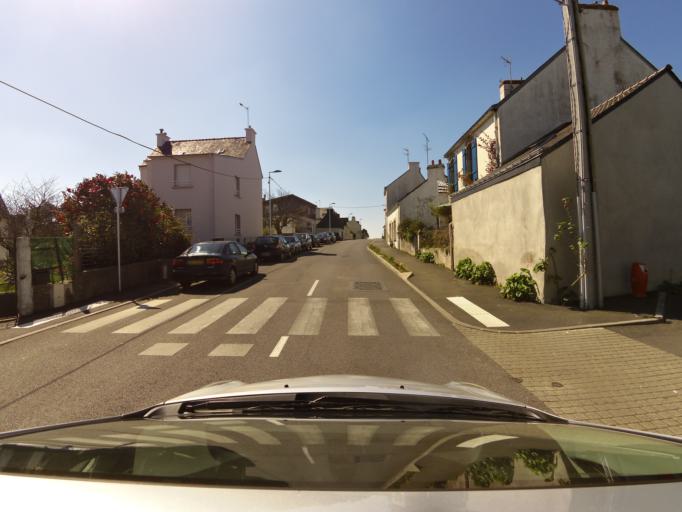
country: FR
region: Brittany
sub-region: Departement du Morbihan
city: Larmor-Plage
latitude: 47.7193
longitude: -3.3849
